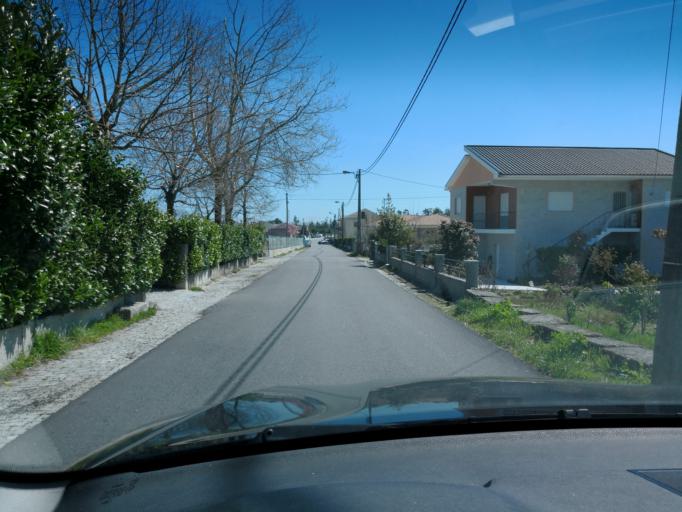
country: PT
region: Vila Real
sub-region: Sabrosa
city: Sabrosa
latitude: 41.3315
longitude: -7.6321
